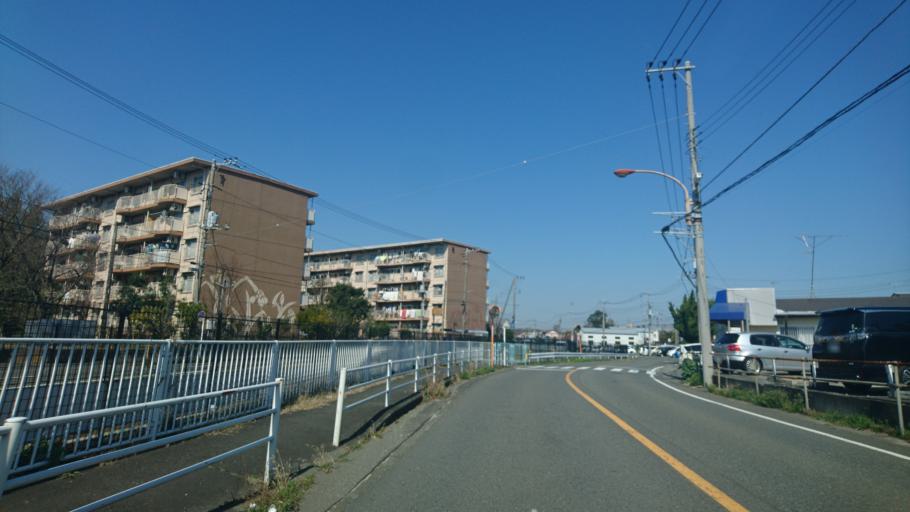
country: JP
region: Kanagawa
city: Fujisawa
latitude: 35.4002
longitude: 139.4454
